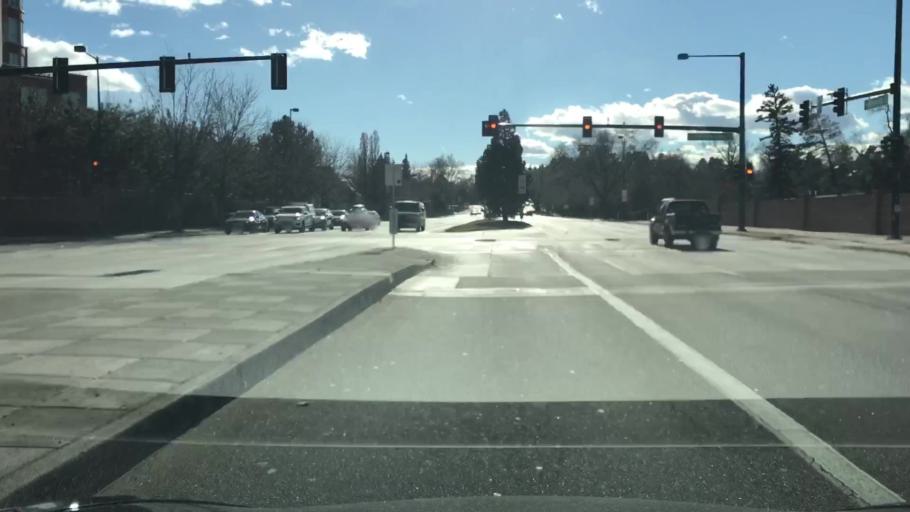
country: US
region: Colorado
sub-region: Arapahoe County
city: Glendale
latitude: 39.7158
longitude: -104.9593
